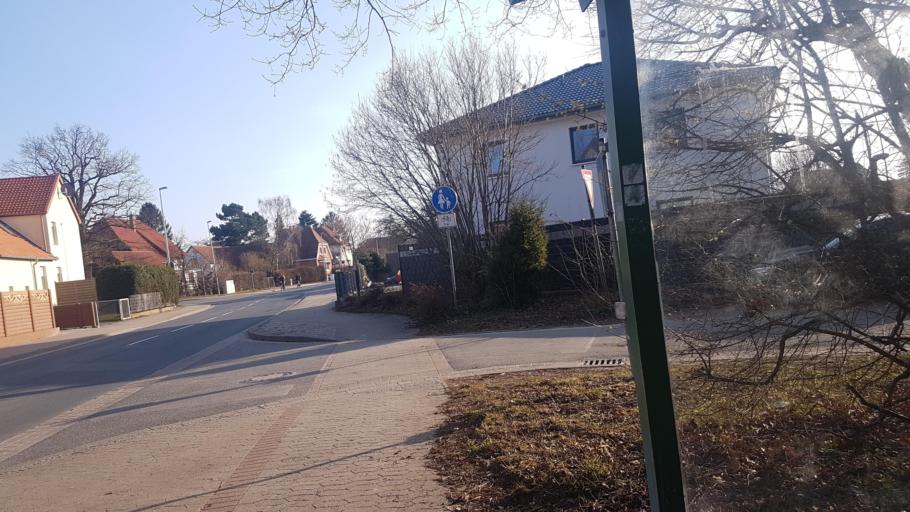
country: DE
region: Lower Saxony
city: Ronnenberg
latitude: 52.3062
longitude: 9.6774
